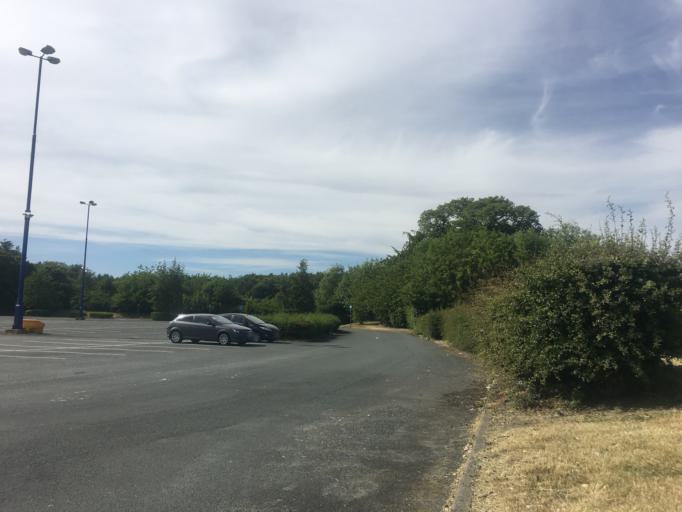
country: GB
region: England
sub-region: Sunderland
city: Washington
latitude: 54.8866
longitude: -1.5395
